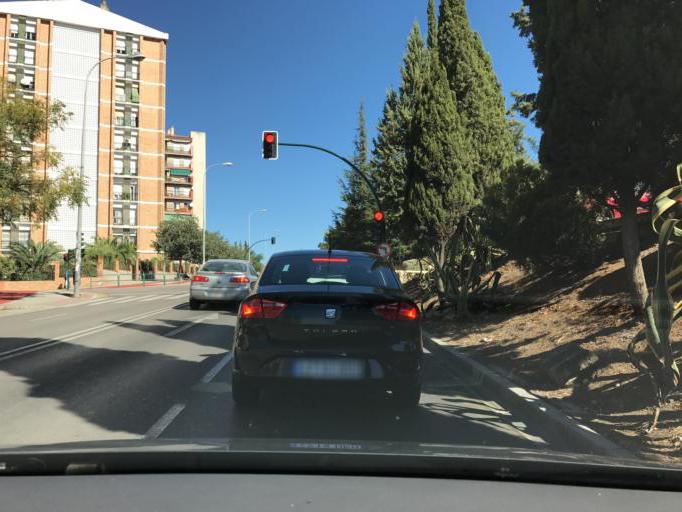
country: ES
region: Andalusia
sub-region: Provincia de Granada
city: Granada
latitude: 37.1971
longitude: -3.6007
